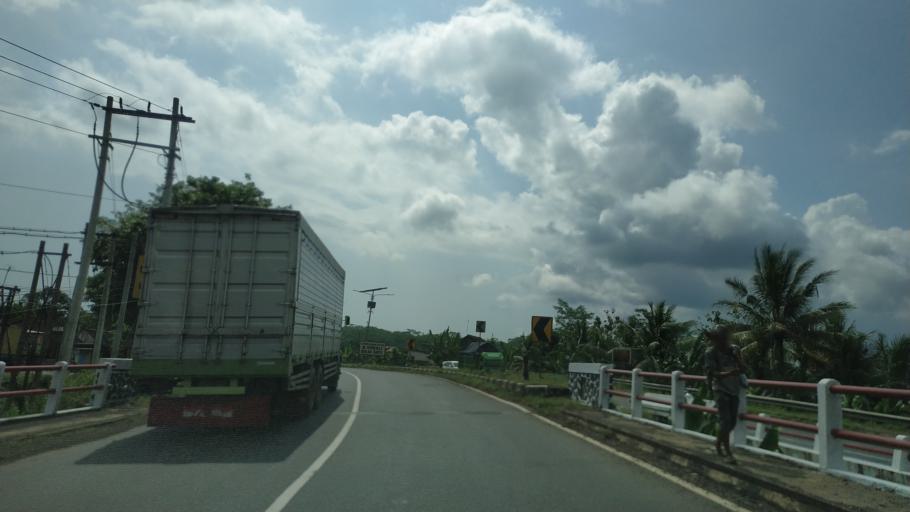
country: ID
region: Central Java
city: Pekalongan
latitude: -6.9525
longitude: 109.8075
